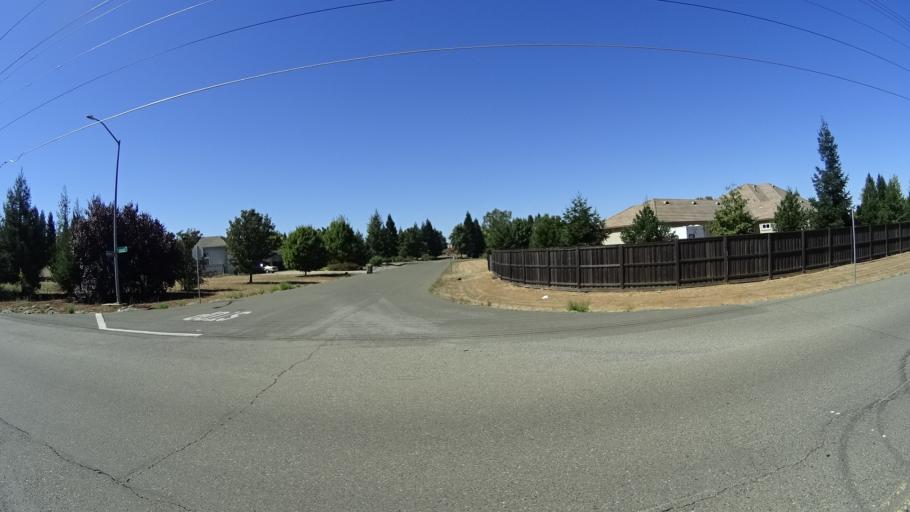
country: US
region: California
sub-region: Sacramento County
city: Wilton
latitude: 38.4426
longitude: -121.2978
